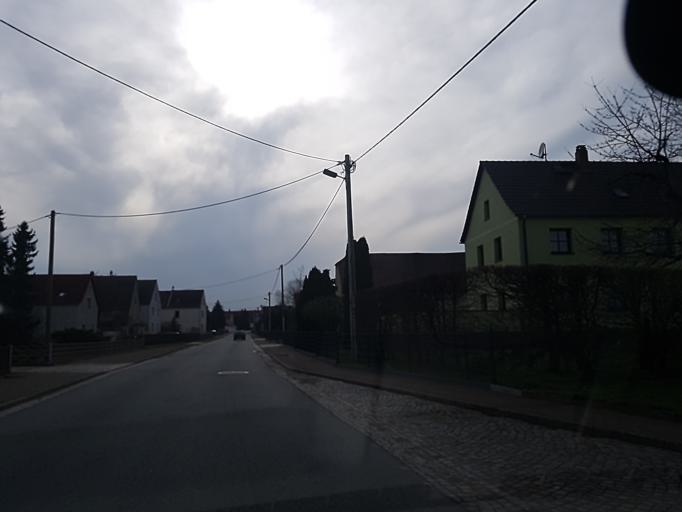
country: DE
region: Saxony
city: Cavertitz
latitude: 51.3667
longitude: 13.1513
